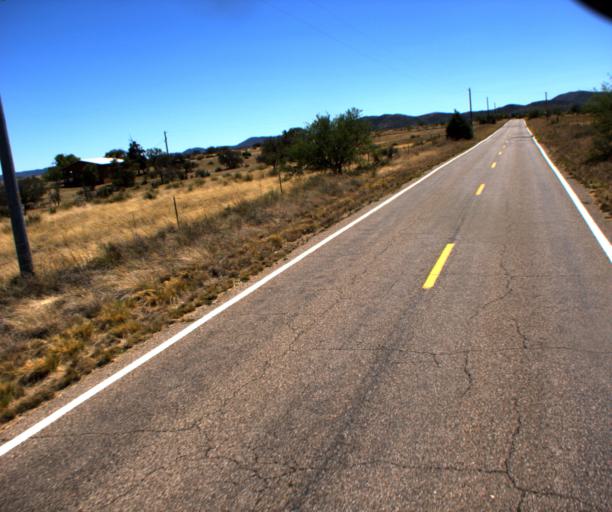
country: US
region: Arizona
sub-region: Cochise County
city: Huachuca City
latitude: 31.5955
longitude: -110.5589
